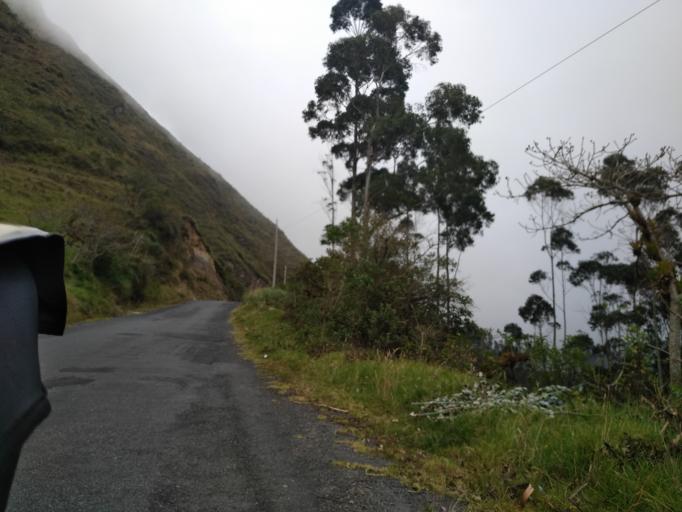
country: EC
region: Cotopaxi
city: Saquisili
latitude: -0.6906
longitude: -78.8266
